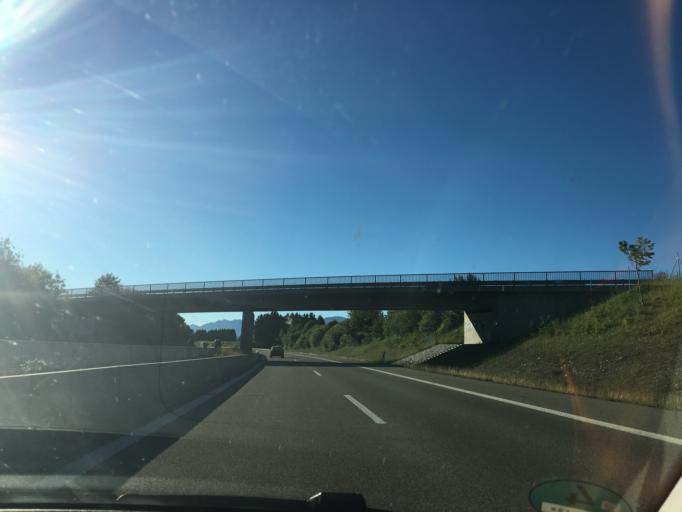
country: DE
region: Bavaria
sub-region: Swabia
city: Seeg
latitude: 47.6292
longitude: 10.5777
